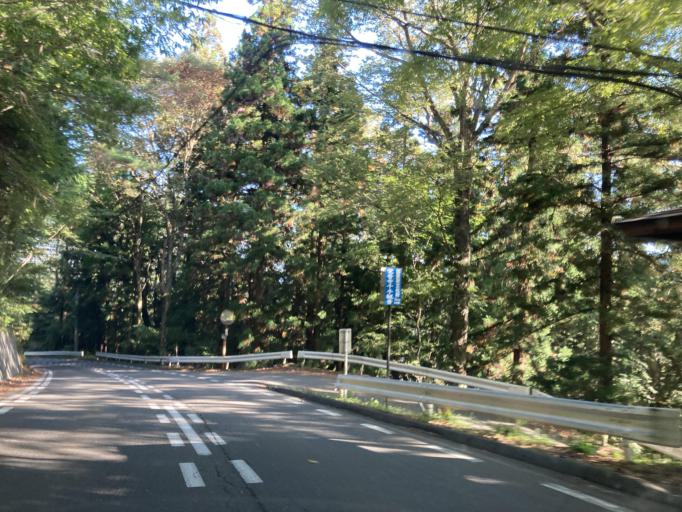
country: JP
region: Nagano
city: Omachi
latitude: 36.4868
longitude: 137.9054
